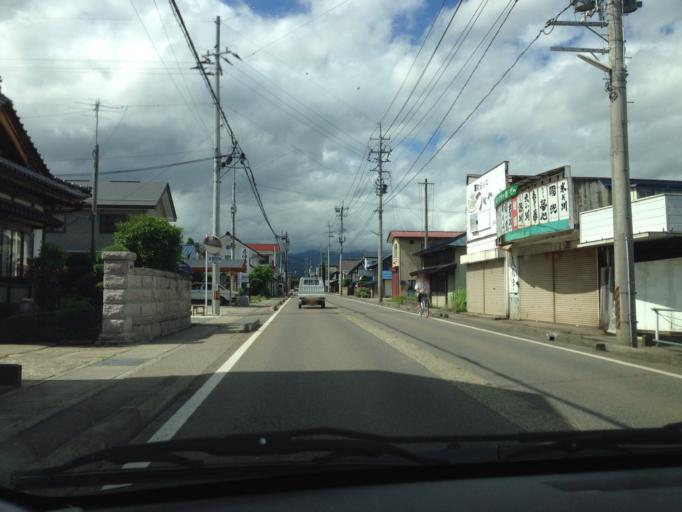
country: JP
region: Fukushima
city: Kitakata
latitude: 37.6721
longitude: 139.8715
